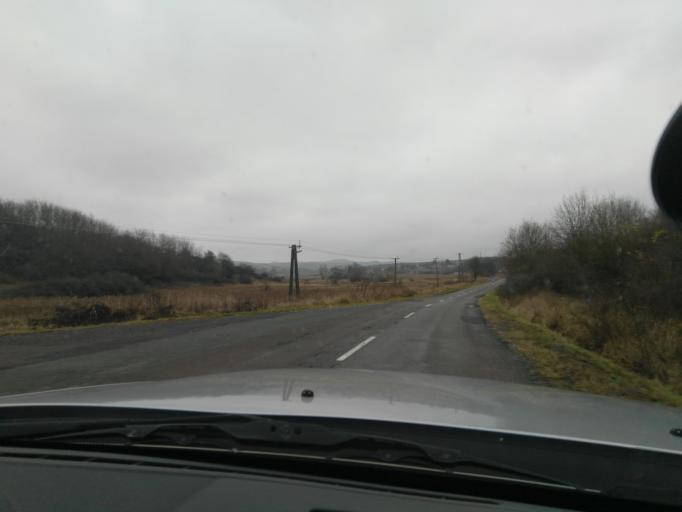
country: HU
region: Nograd
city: Matraterenye
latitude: 48.0436
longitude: 19.9182
